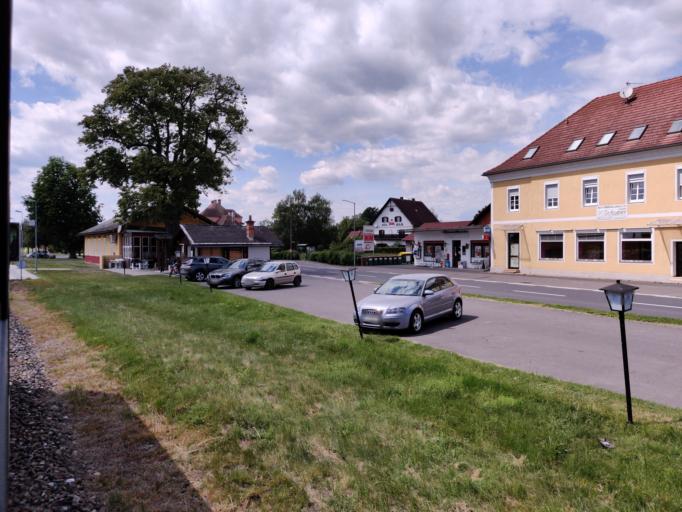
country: SI
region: Apace
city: Apace
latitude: 46.7316
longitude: 15.9043
